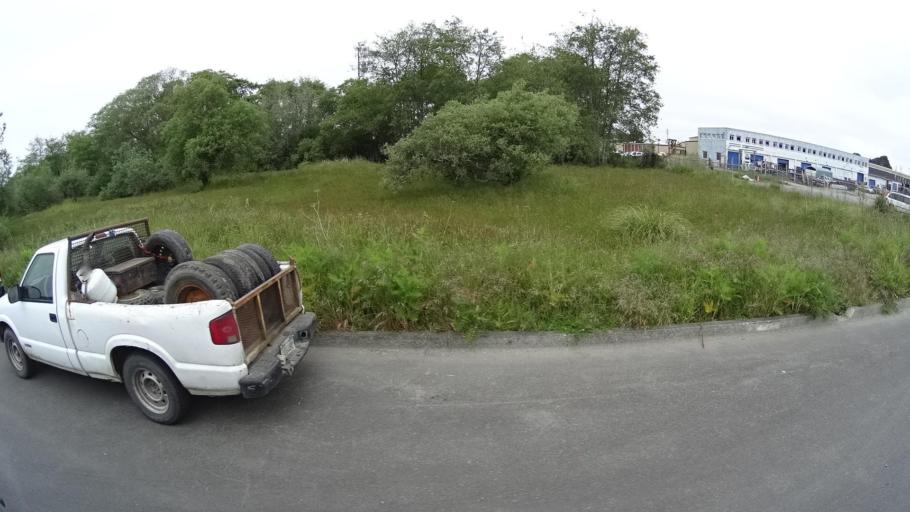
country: US
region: California
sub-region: Humboldt County
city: Bayview
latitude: 40.7892
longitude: -124.1818
